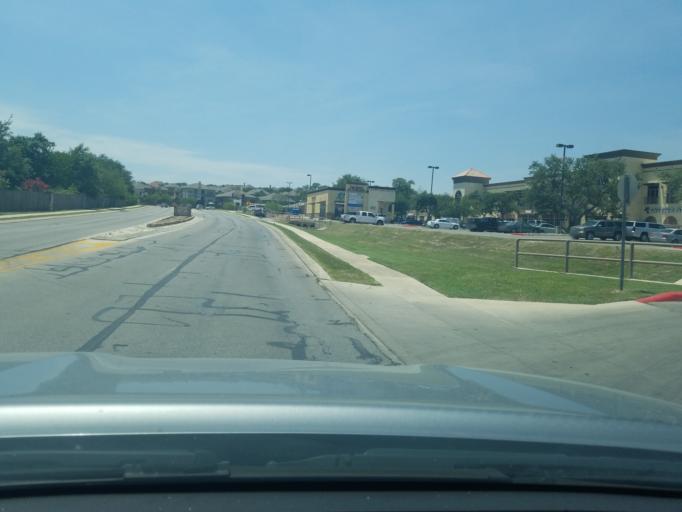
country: US
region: Texas
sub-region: Bexar County
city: Timberwood Park
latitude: 29.6849
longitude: -98.4723
